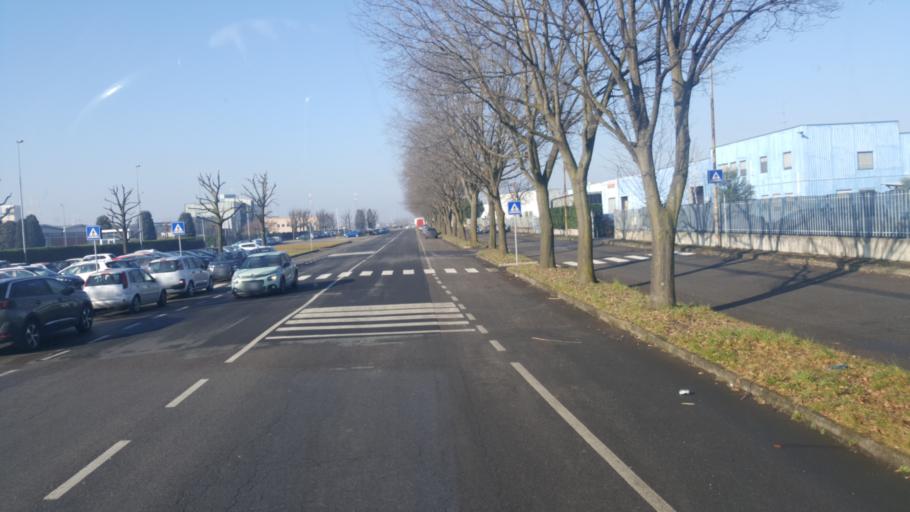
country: IT
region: Lombardy
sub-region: Citta metropolitana di Milano
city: Marcallo
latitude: 45.4789
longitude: 8.8689
